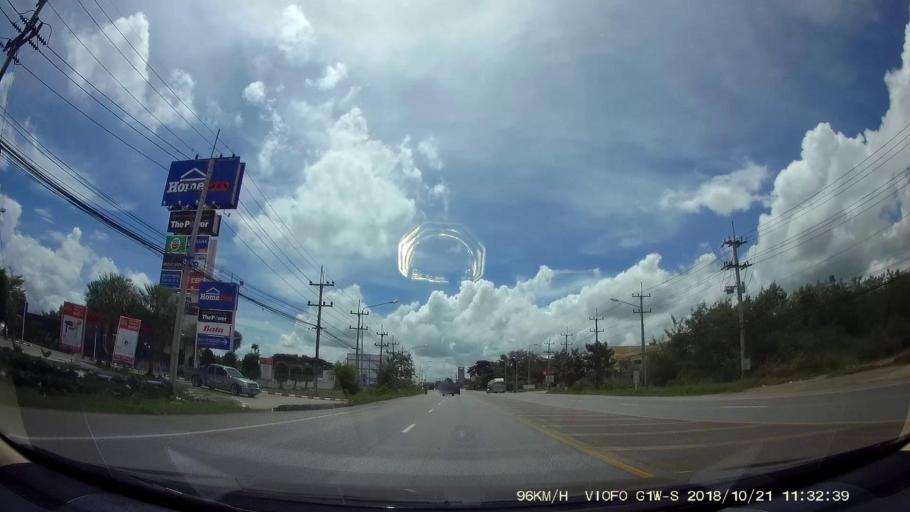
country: TH
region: Chaiyaphum
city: Chaiyaphum
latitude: 15.7554
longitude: 102.0241
